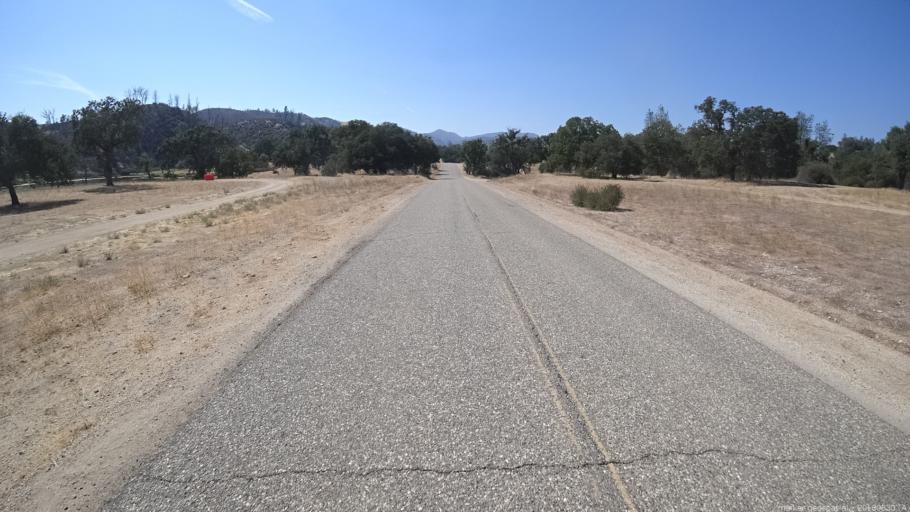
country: US
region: California
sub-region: Monterey County
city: King City
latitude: 36.0015
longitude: -121.2598
